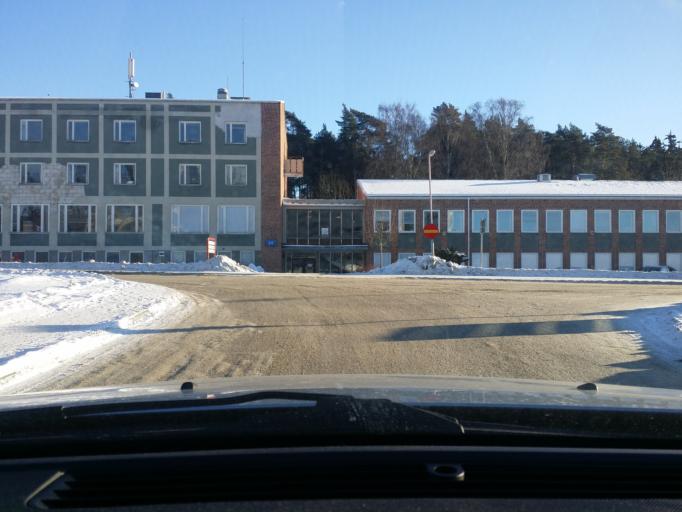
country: SE
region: Vaestmanland
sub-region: Vasteras
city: Vasteras
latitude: 59.6165
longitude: 16.5842
